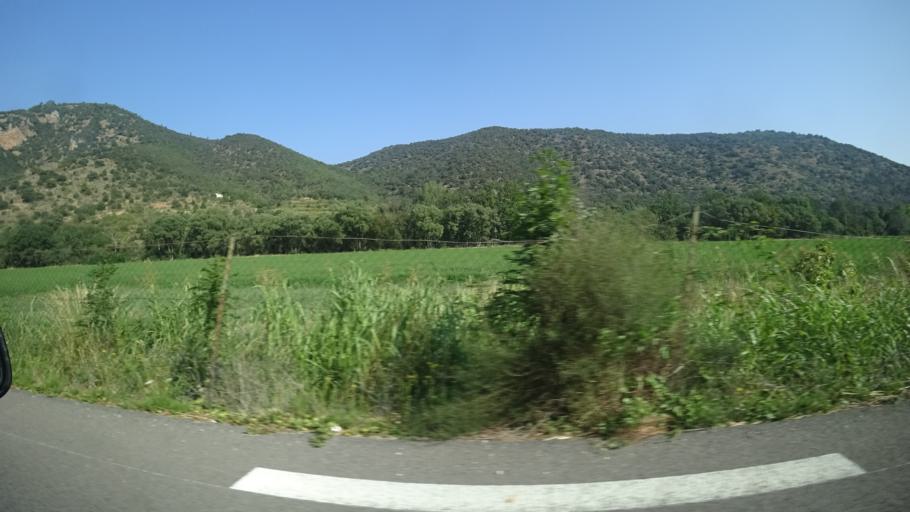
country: FR
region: Languedoc-Roussillon
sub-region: Departement des Pyrenees-Orientales
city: Ria-Sirach
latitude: 42.6025
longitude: 2.3862
